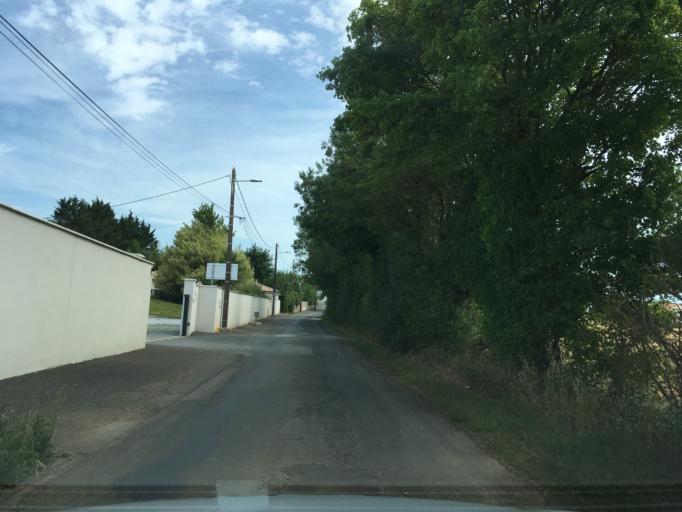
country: FR
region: Poitou-Charentes
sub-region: Departement des Deux-Sevres
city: Aiffres
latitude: 46.3004
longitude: -0.4363
